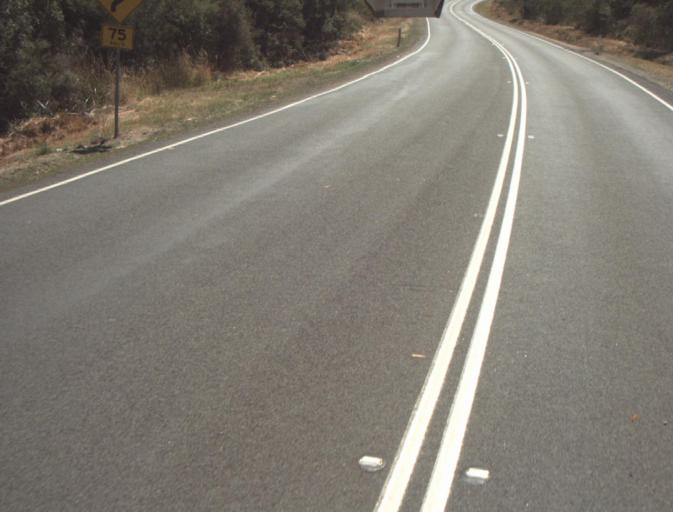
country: AU
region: Tasmania
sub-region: Launceston
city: Mayfield
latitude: -41.3589
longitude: 147.1430
